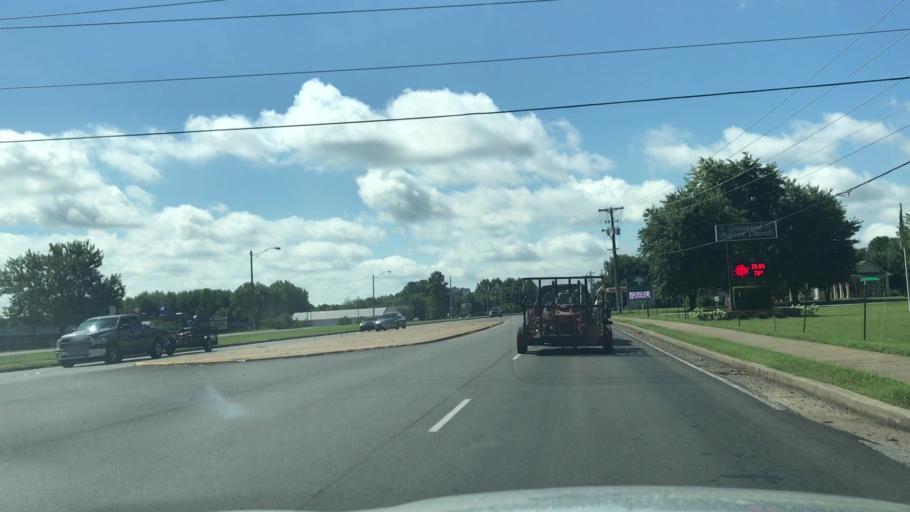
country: US
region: Kentucky
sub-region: Warren County
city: Plano
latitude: 36.9259
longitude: -86.4114
